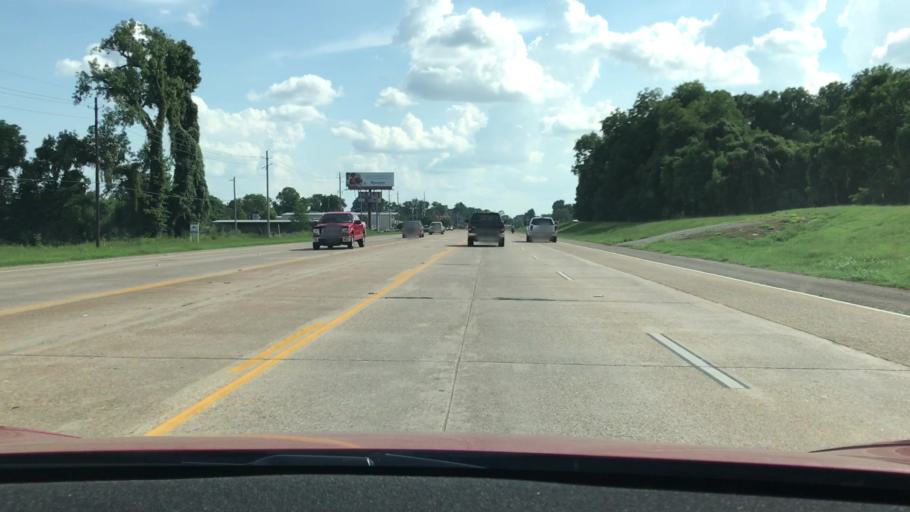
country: US
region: Louisiana
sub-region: Bossier Parish
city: Bossier City
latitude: 32.4544
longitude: -93.6929
